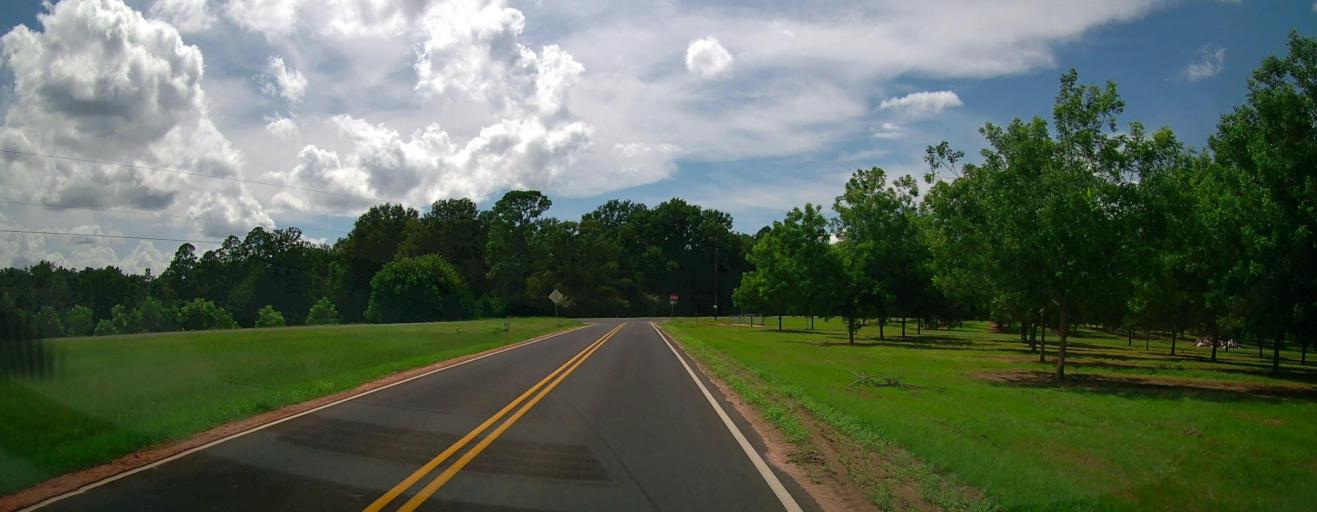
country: US
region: Georgia
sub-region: Macon County
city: Marshallville
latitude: 32.4567
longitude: -83.9220
